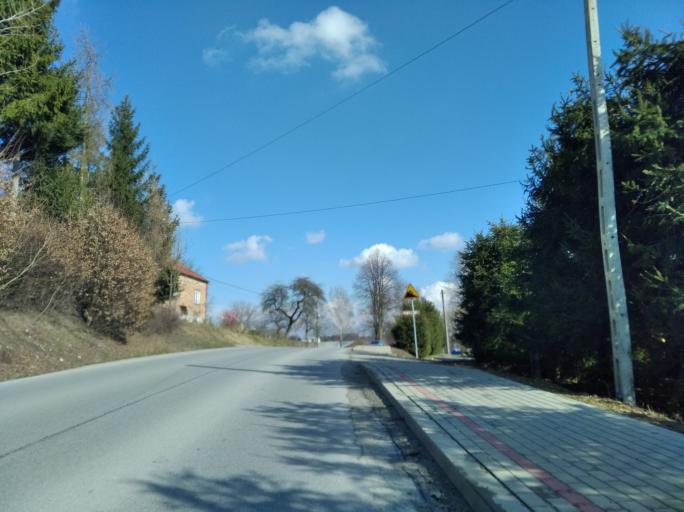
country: PL
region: Subcarpathian Voivodeship
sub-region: Powiat strzyzowski
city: Frysztak
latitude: 49.8448
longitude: 21.5673
